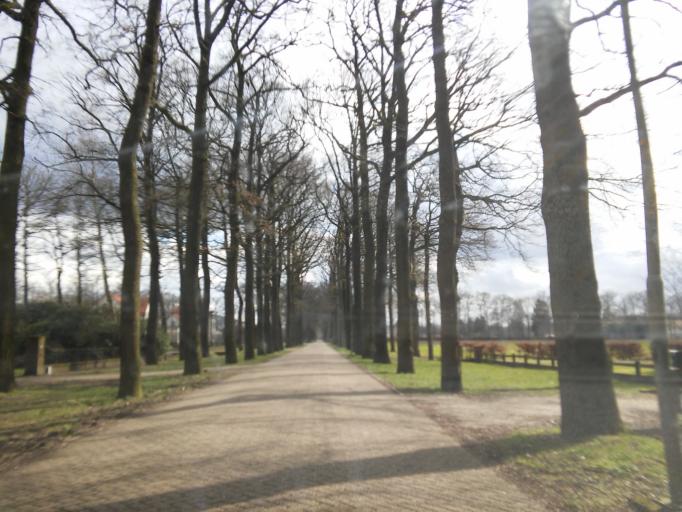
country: BE
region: Flanders
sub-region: Provincie Antwerpen
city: Merksplas
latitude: 51.4005
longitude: 4.8251
